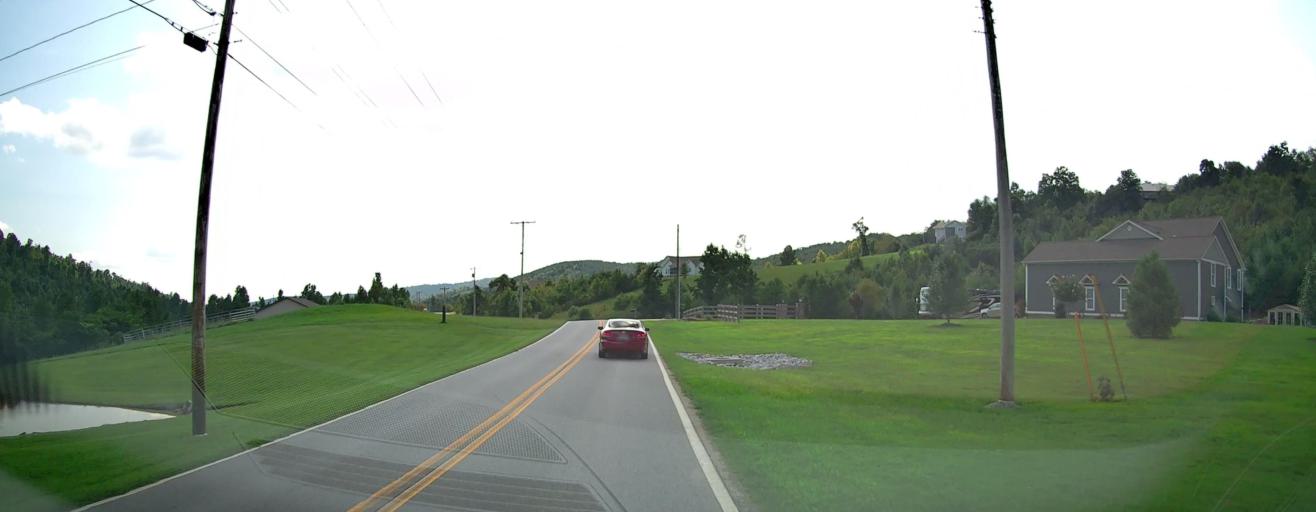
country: US
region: Georgia
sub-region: Catoosa County
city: Ringgold
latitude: 34.9538
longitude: -85.0758
